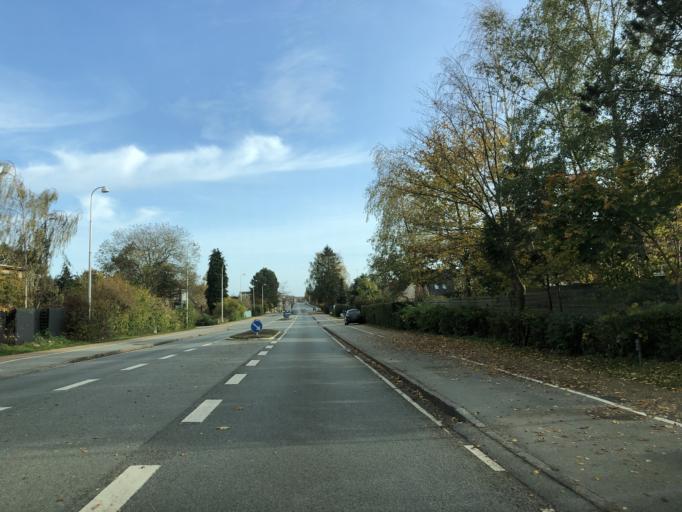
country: DK
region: Capital Region
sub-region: Rudersdal Kommune
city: Birkerod
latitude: 55.8464
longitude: 12.4302
